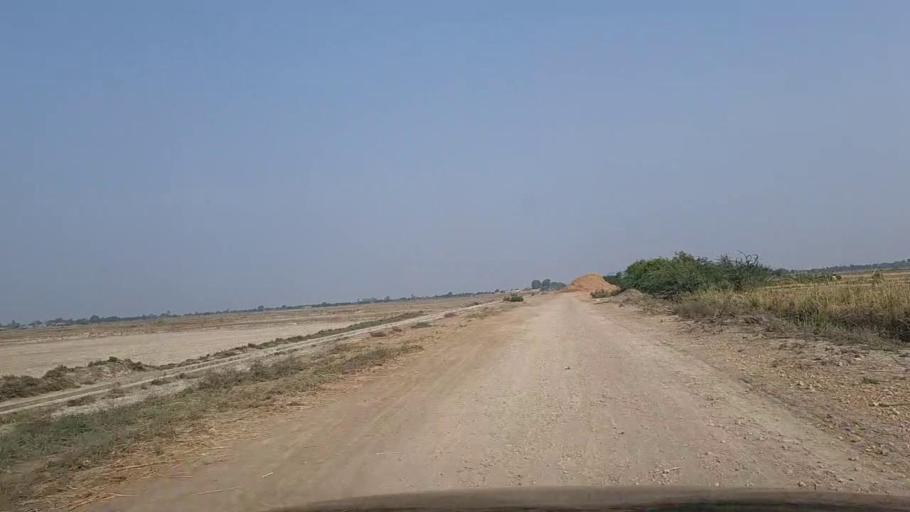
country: PK
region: Sindh
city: Thatta
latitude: 24.7601
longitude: 67.8715
